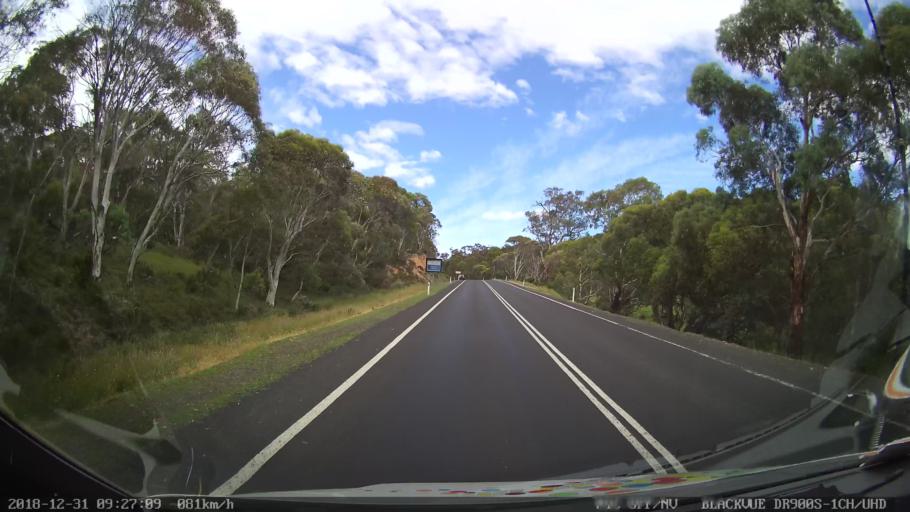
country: AU
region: New South Wales
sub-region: Snowy River
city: Jindabyne
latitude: -36.4546
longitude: 148.4885
